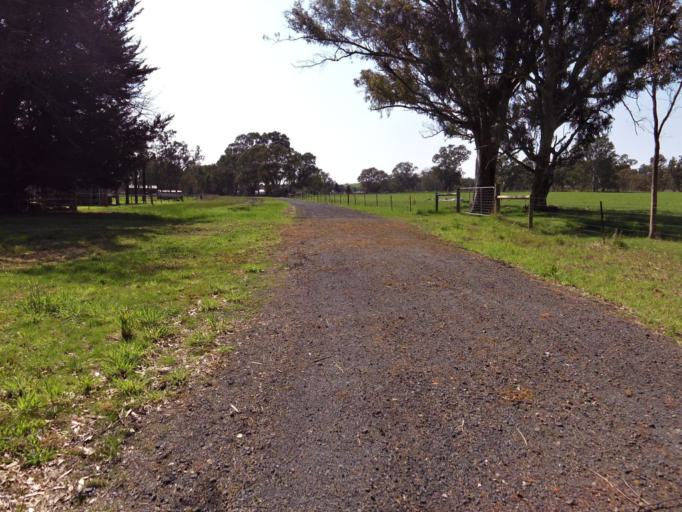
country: AU
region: Victoria
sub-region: Murrindindi
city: Alexandra
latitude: -37.1106
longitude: 145.6113
